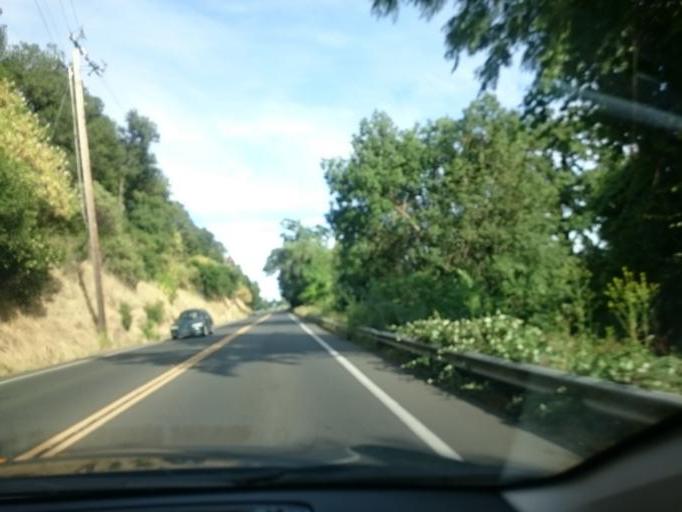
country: US
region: California
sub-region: Napa County
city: Saint Helena
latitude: 38.5187
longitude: -122.4663
